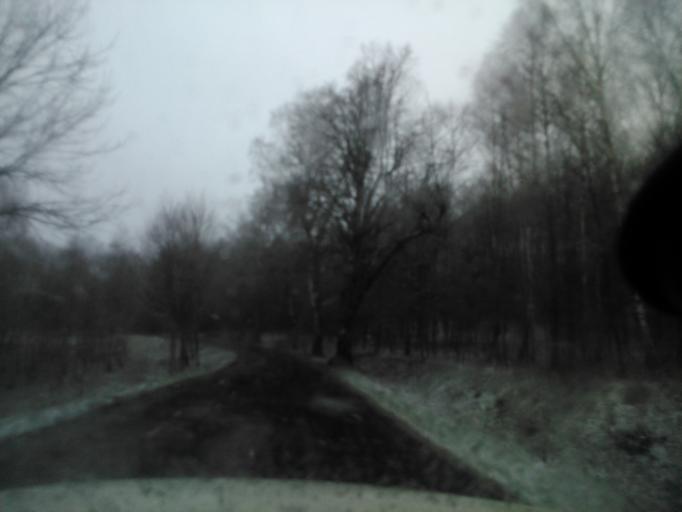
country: PL
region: Warmian-Masurian Voivodeship
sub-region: Powiat ostrodzki
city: Dabrowno
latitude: 53.3886
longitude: 20.0140
